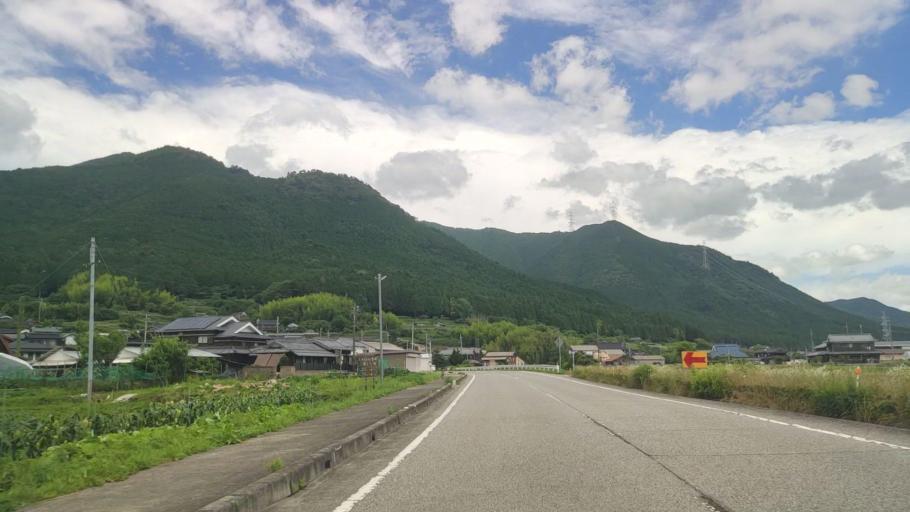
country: JP
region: Hyogo
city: Nishiwaki
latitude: 35.1449
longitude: 134.9262
